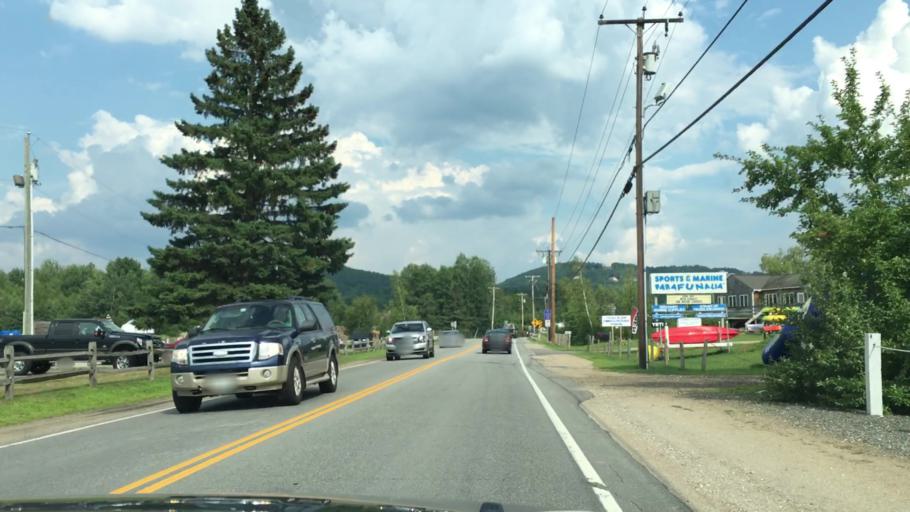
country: US
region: New Hampshire
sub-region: Belknap County
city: Gilford
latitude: 43.5789
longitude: -71.4052
